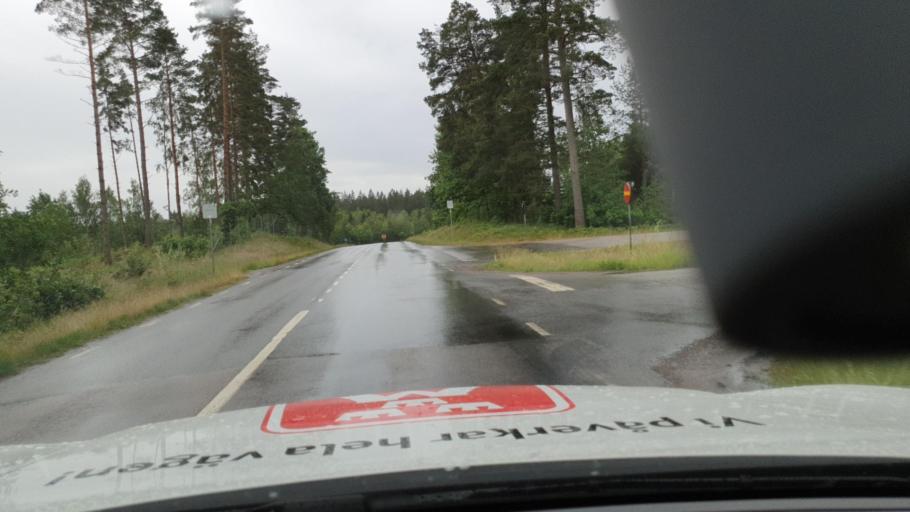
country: SE
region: Vaestra Goetaland
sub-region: Mariestads Kommun
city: Mariestad
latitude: 58.7292
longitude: 13.8926
